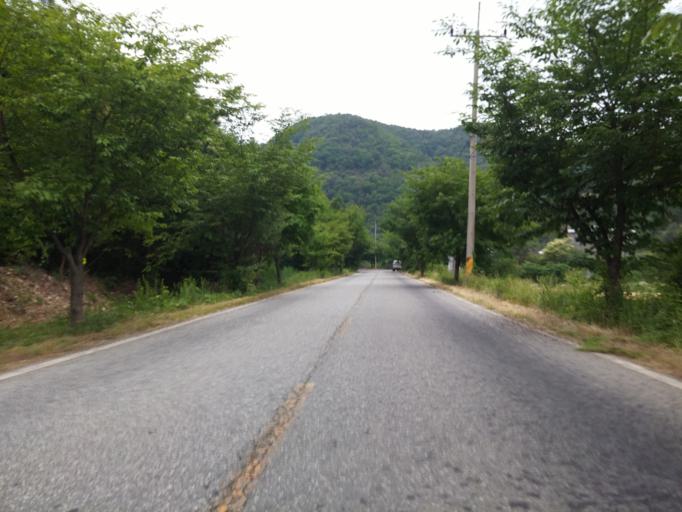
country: KR
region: Chungcheongbuk-do
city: Okcheon
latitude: 36.2007
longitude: 127.5670
